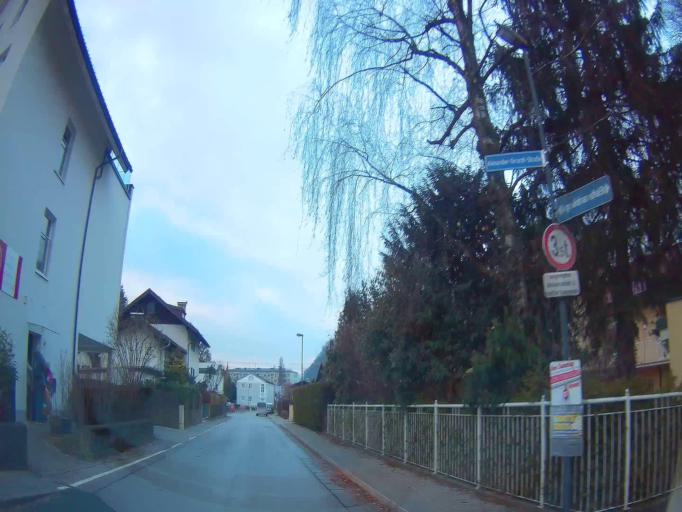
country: AT
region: Salzburg
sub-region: Salzburg Stadt
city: Salzburg
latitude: 47.8043
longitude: 13.0729
